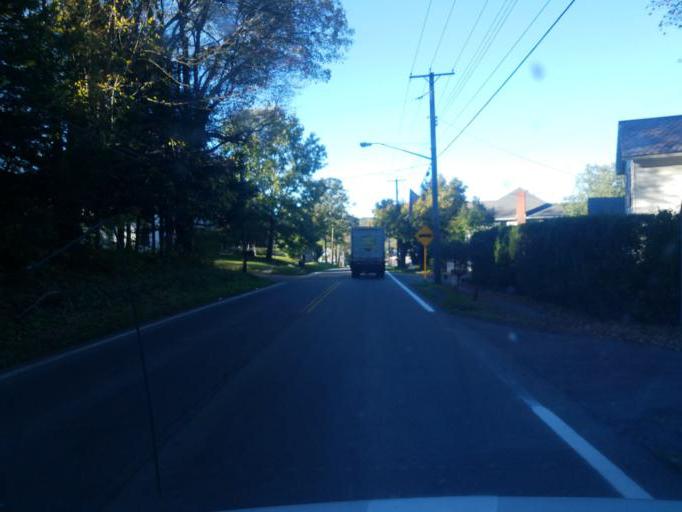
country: US
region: Ohio
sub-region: Columbiana County
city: New Waterford
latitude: 40.7900
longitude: -80.6255
